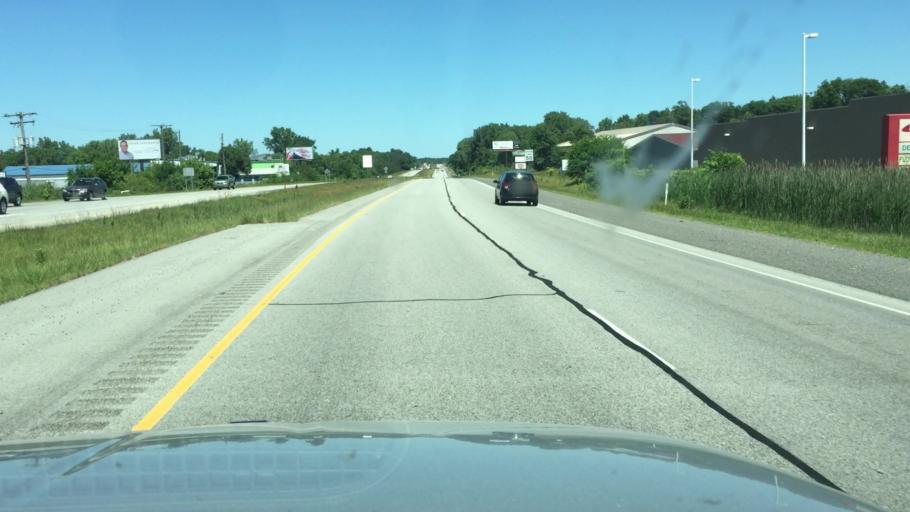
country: US
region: Indiana
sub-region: Porter County
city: Chesterton
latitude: 41.5946
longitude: -87.0453
